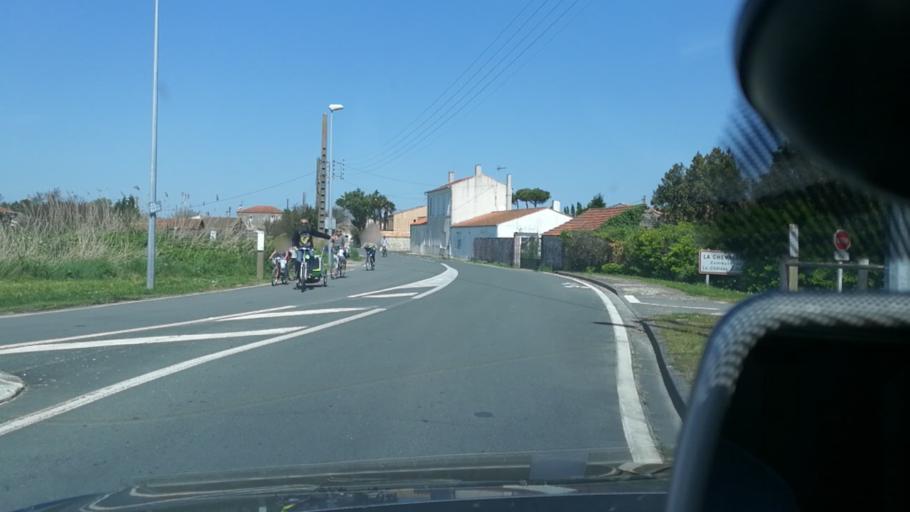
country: FR
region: Poitou-Charentes
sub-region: Departement de la Charente-Maritime
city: Saint-Trojan-les-Bains
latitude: 45.8714
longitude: -1.2175
